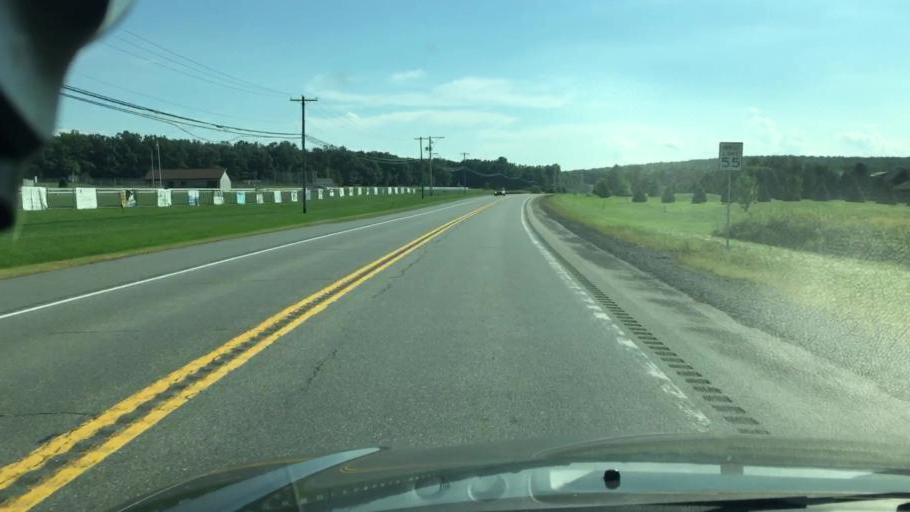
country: US
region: Pennsylvania
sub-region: Carbon County
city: Jim Thorpe
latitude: 40.9331
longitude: -75.6583
